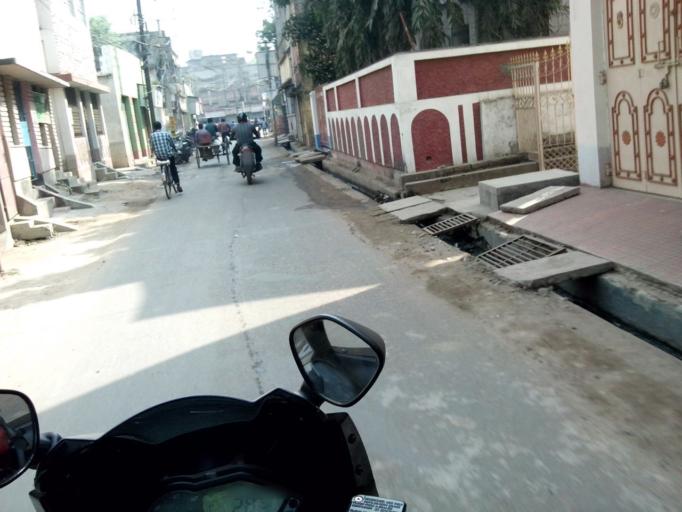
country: IN
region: West Bengal
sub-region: Barddhaman
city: Barddhaman
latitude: 23.2356
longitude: 87.8662
